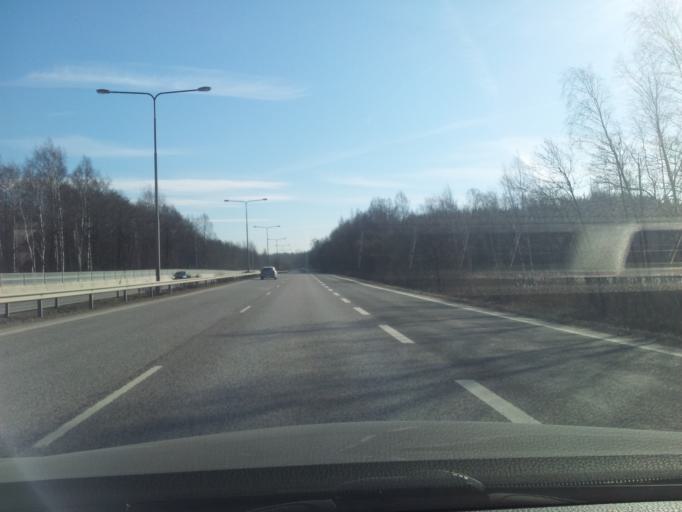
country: FI
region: Uusimaa
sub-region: Helsinki
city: Teekkarikylae
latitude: 60.2046
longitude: 24.8504
